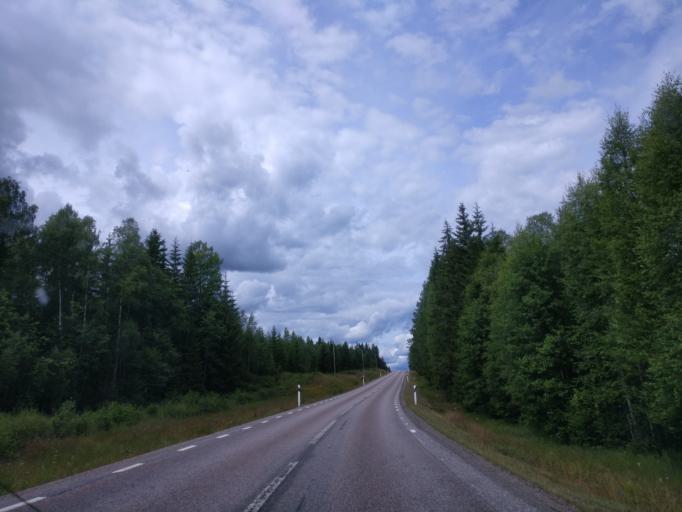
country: SE
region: Vaermland
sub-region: Hagfors Kommun
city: Ekshaerad
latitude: 60.1799
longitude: 13.3546
